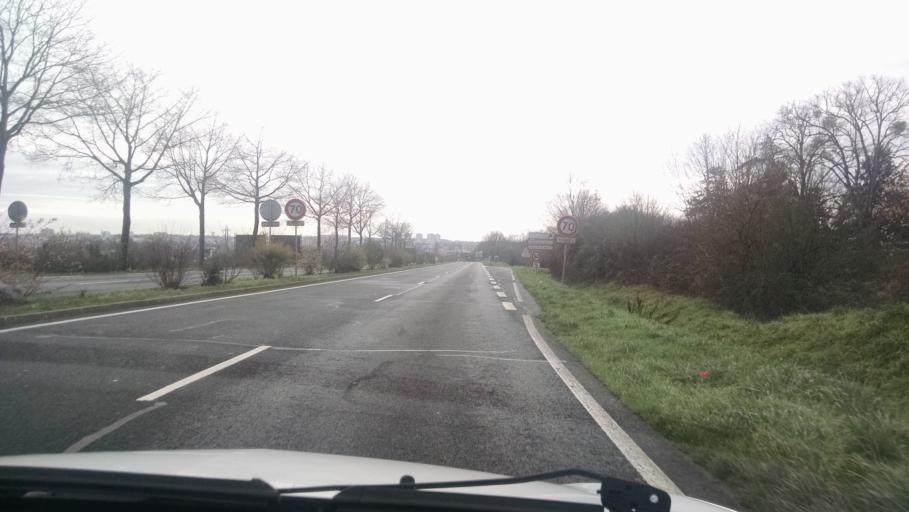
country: FR
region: Pays de la Loire
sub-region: Departement de Maine-et-Loire
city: Cholet
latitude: 47.0635
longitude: -0.9054
